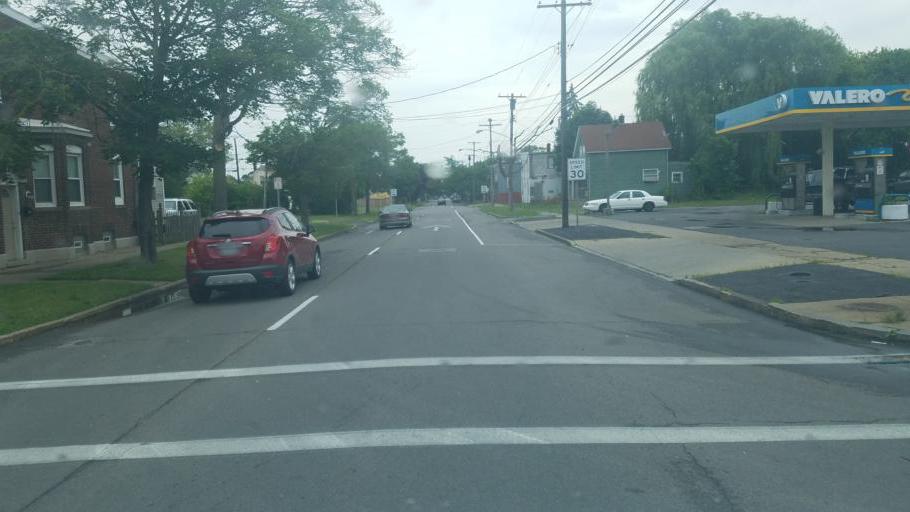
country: US
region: New York
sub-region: Niagara County
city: Niagara Falls
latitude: 43.0915
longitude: -79.0389
